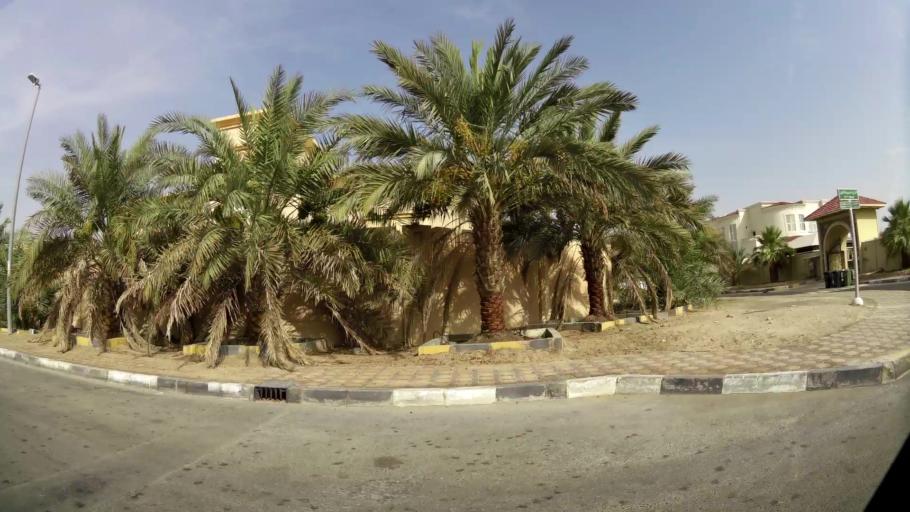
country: AE
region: Abu Dhabi
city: Al Ain
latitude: 24.1390
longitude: 55.7056
